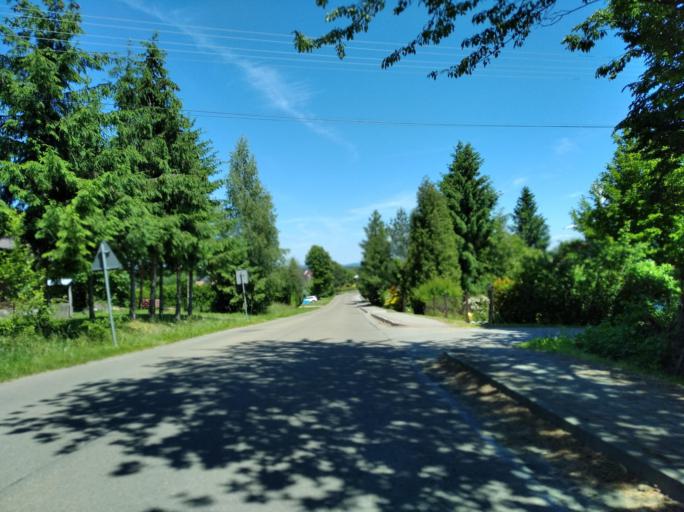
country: PL
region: Subcarpathian Voivodeship
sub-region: Powiat jasielski
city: Tarnowiec
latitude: 49.7165
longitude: 21.5548
